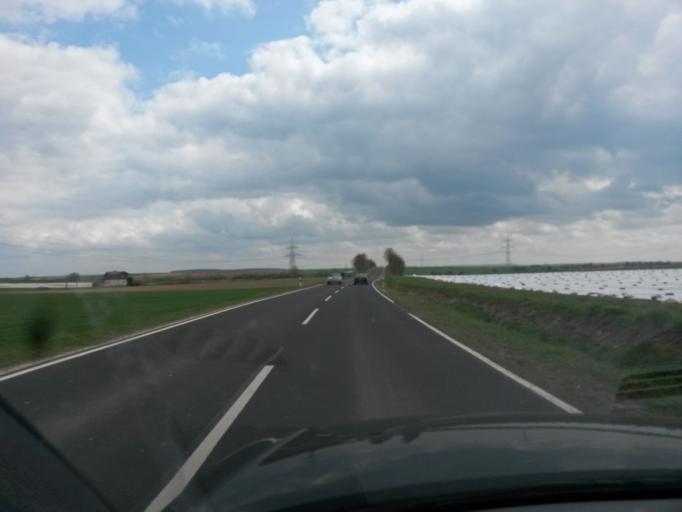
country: DE
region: Bavaria
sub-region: Regierungsbezirk Unterfranken
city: Oberpleichfeld
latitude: 49.8747
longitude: 10.0946
